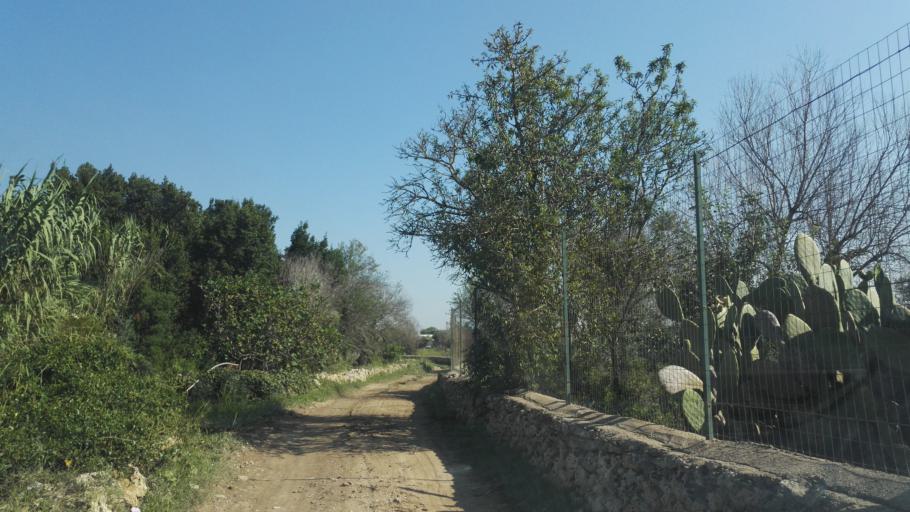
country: IT
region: Apulia
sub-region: Provincia di Lecce
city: Alezio
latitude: 40.0520
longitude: 18.0394
